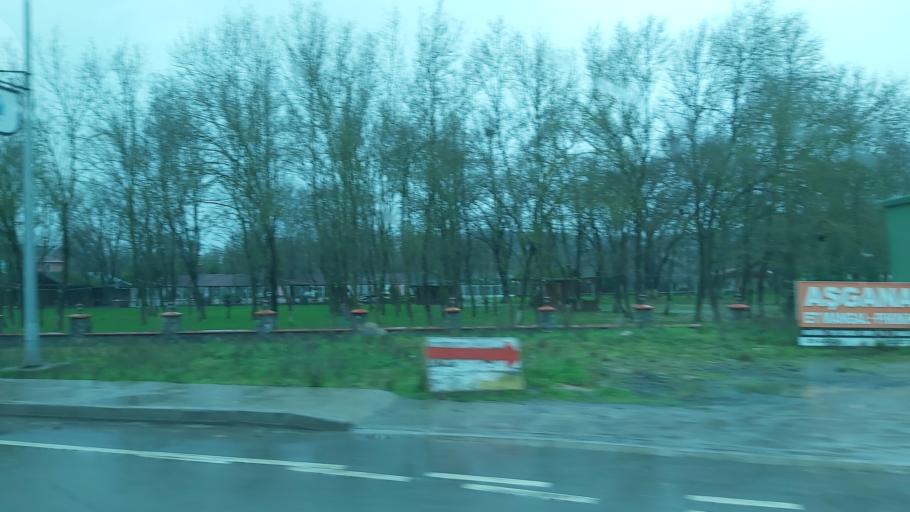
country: TR
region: Istanbul
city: Mahmut Sevket Pasa
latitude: 41.1158
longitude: 29.3040
